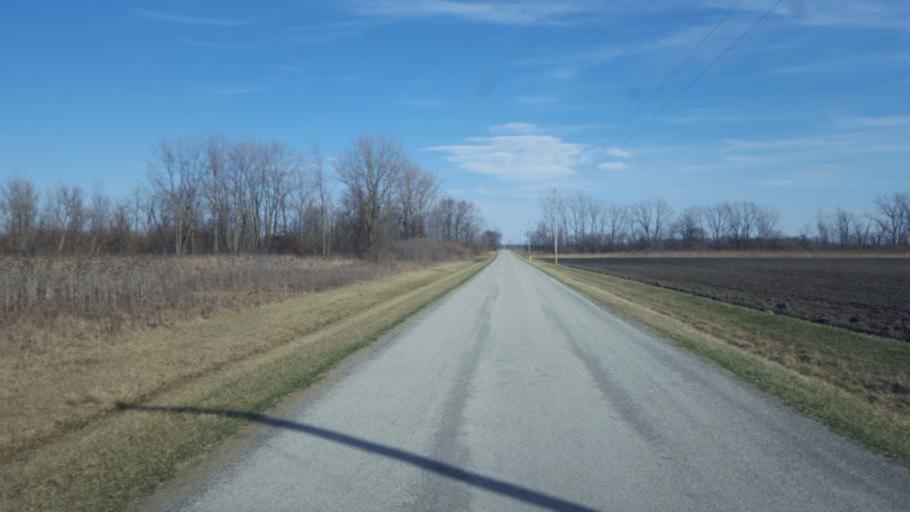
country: US
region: Ohio
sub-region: Wyandot County
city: Upper Sandusky
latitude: 40.7020
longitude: -83.2985
